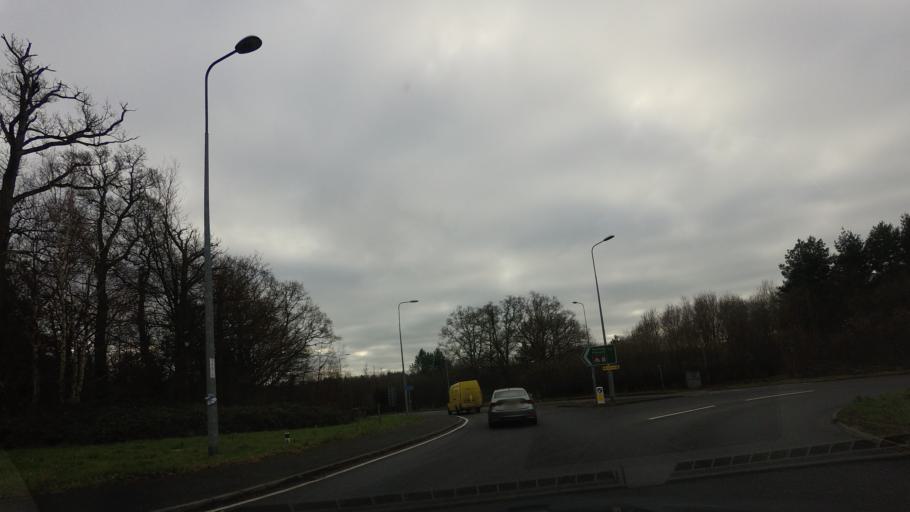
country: GB
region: England
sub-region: East Sussex
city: Wadhurst
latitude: 51.0913
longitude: 0.3961
